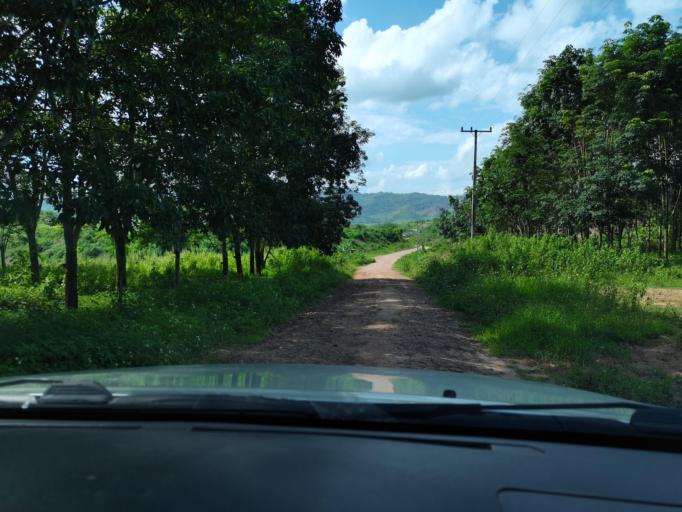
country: LA
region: Loungnamtha
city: Muang Nale
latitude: 20.5810
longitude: 101.0595
